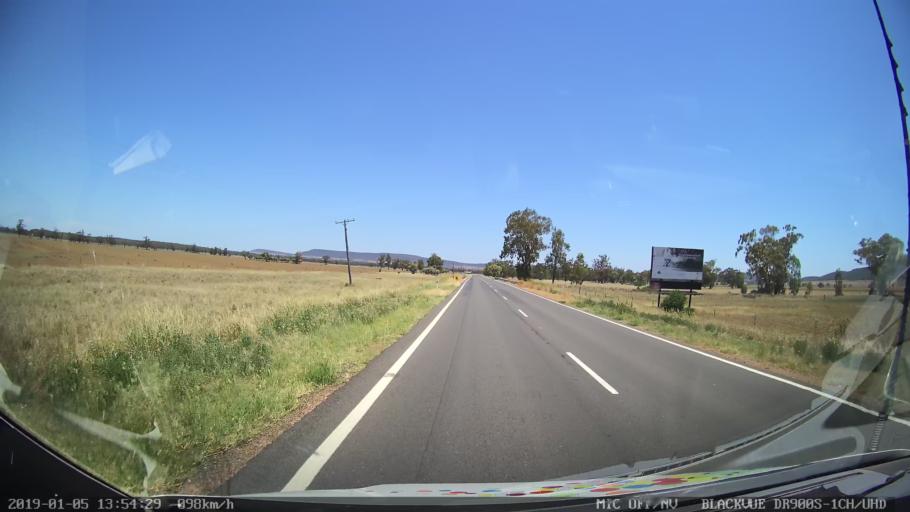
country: AU
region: New South Wales
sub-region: Gunnedah
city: Gunnedah
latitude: -31.0895
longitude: 150.2738
